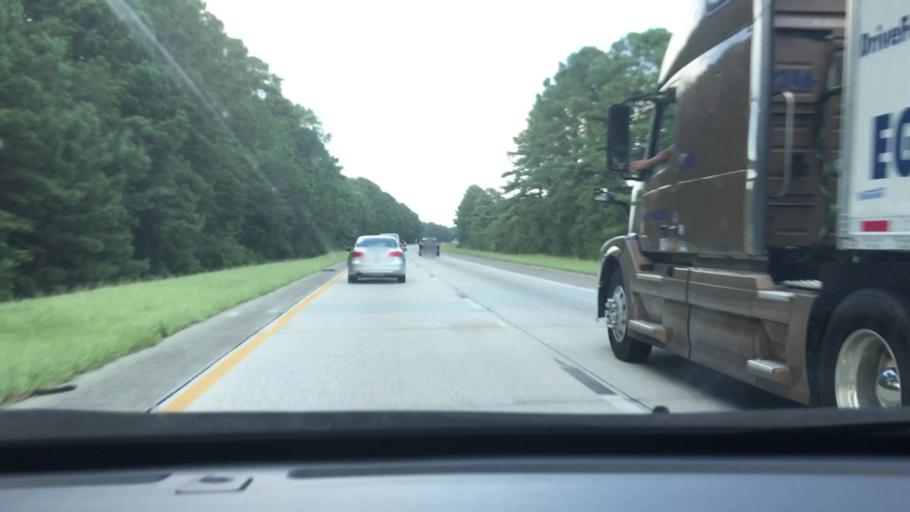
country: US
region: South Carolina
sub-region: Florence County
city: Timmonsville
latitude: 34.0582
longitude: -79.9682
